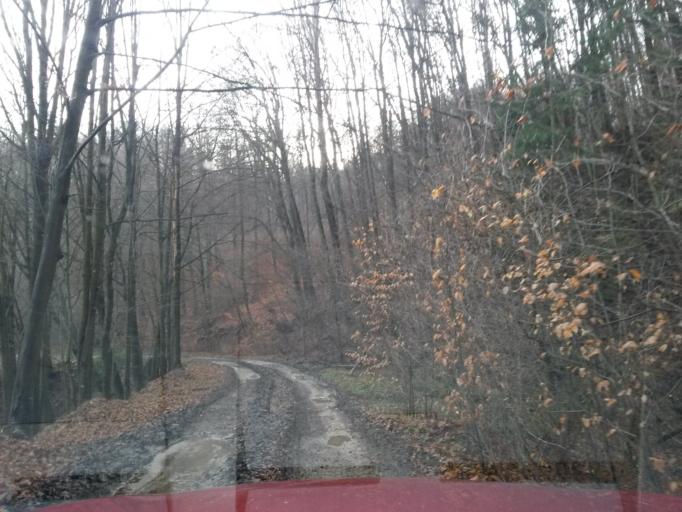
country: SK
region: Kosicky
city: Dobsina
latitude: 48.7432
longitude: 20.4059
